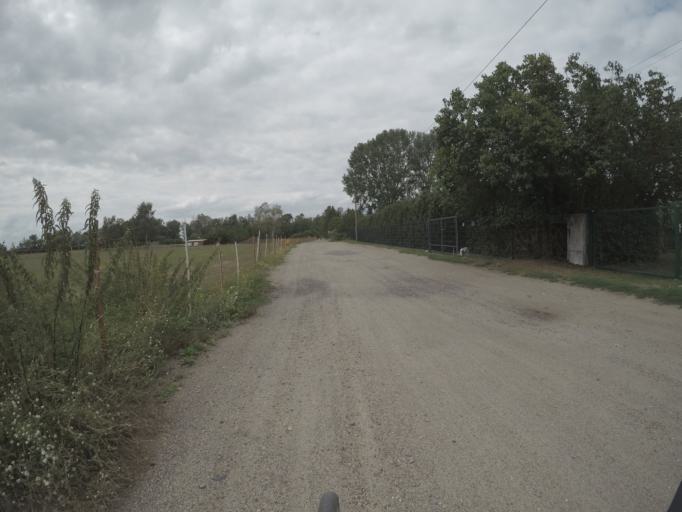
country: DE
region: Brandenburg
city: Nauen
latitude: 52.6079
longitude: 12.9262
